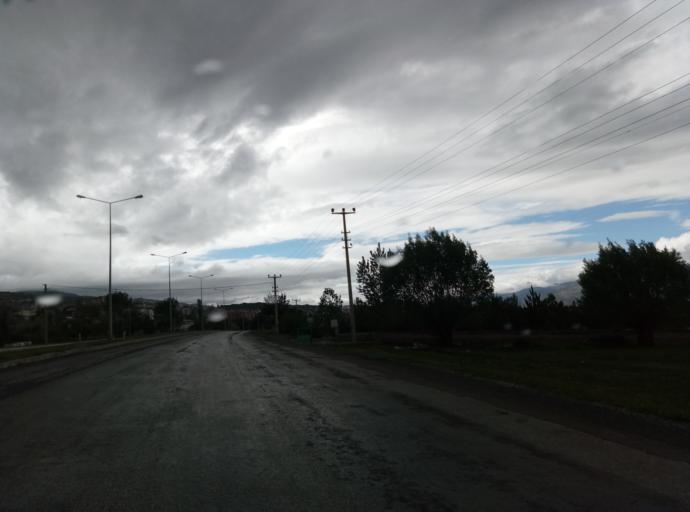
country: TR
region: Sivas
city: Susehri
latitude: 40.1691
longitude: 38.0966
